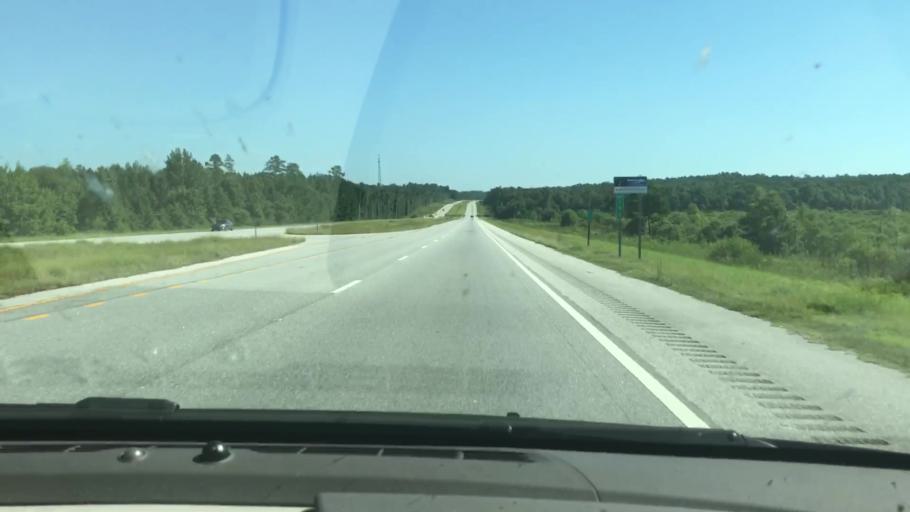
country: US
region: Alabama
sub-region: Russell County
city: Ladonia
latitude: 32.3759
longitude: -85.0880
